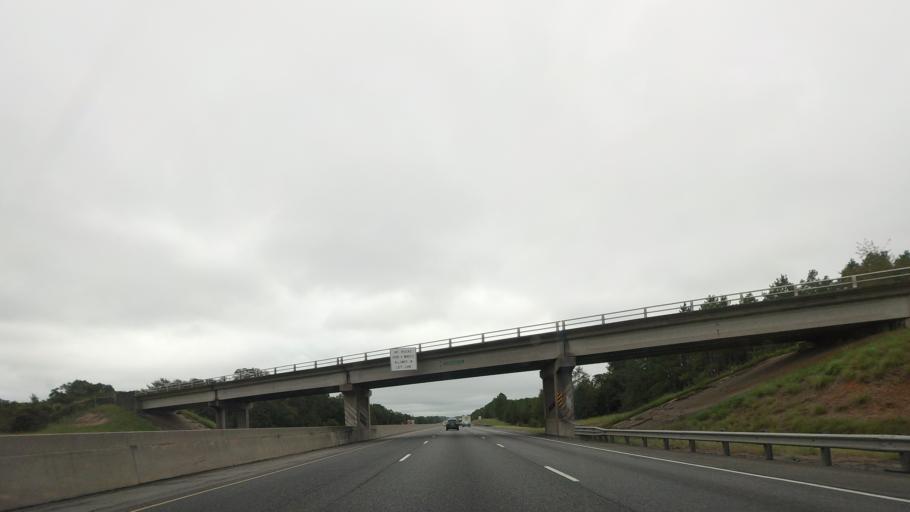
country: US
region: Georgia
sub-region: Turner County
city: Ashburn
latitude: 31.7885
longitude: -83.6921
